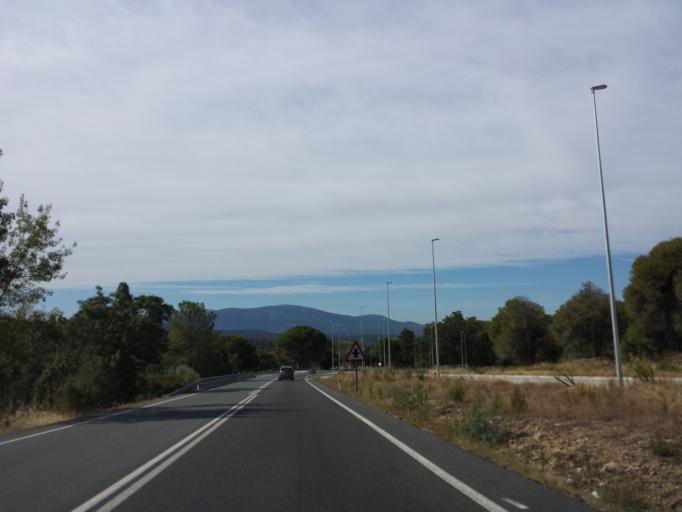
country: ES
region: Castille and Leon
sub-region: Provincia de Avila
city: Piedralaves
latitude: 40.2960
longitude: -4.7213
